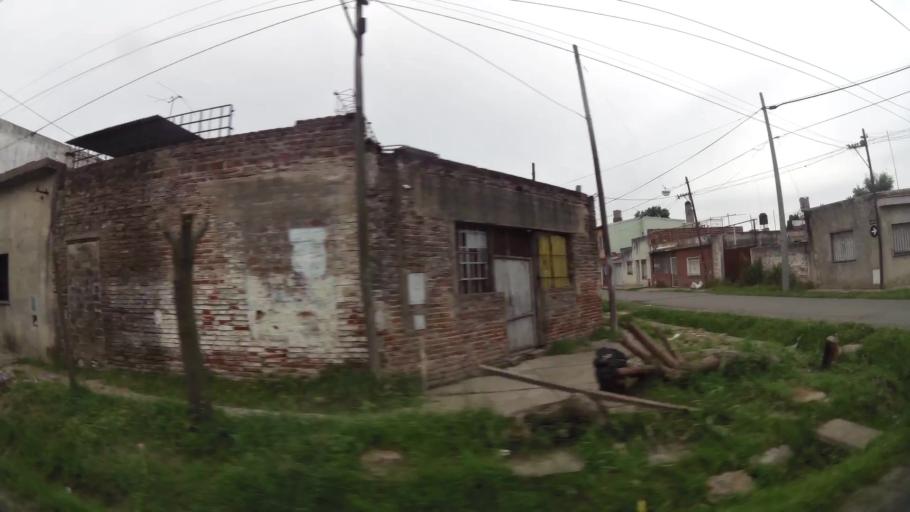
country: AR
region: Santa Fe
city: Granadero Baigorria
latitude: -32.8982
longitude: -60.7028
